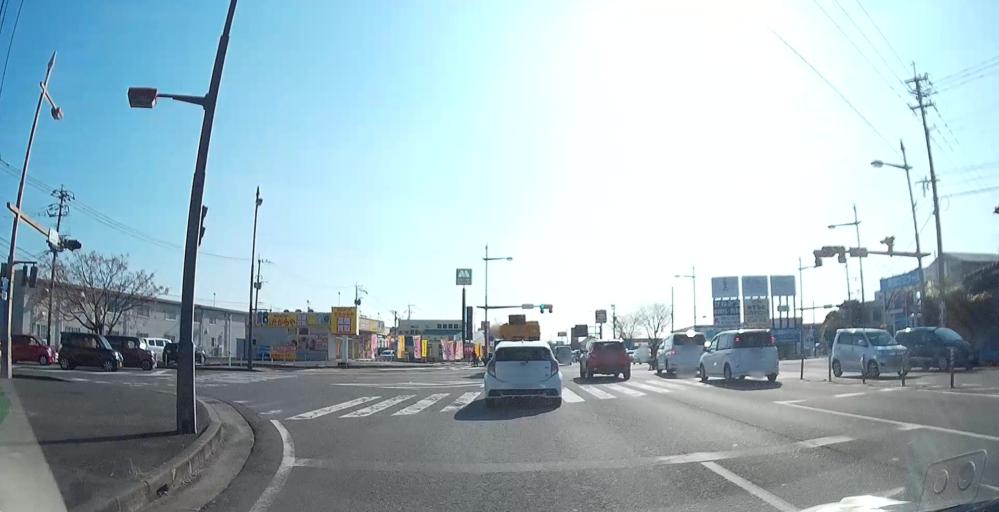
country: JP
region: Kumamoto
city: Kumamoto
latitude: 32.7839
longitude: 130.6734
